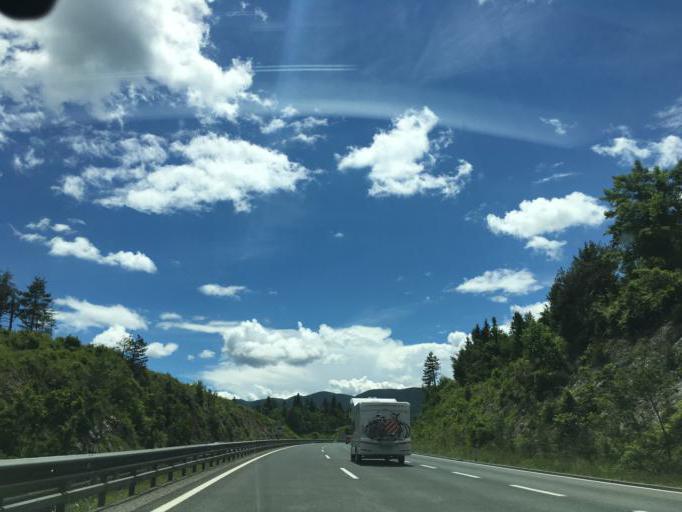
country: SI
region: Cerknica
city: Rakek
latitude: 45.8154
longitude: 14.2860
